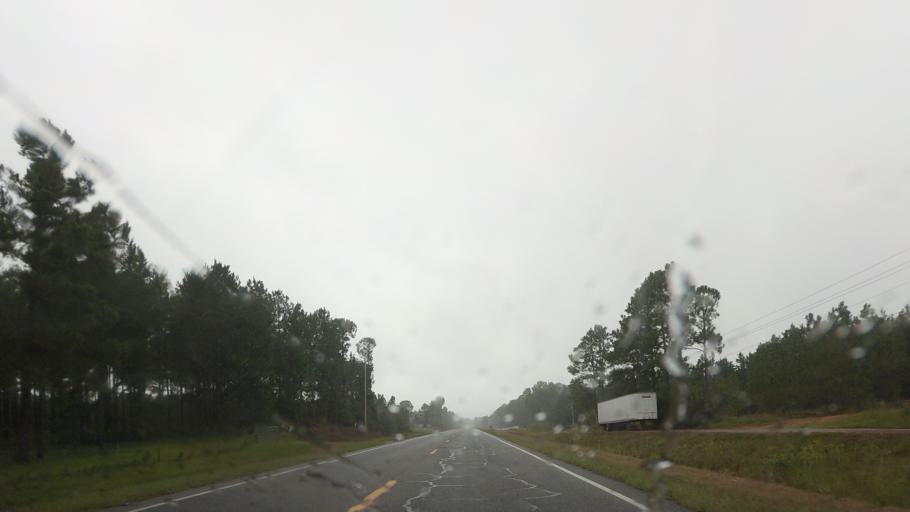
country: US
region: Georgia
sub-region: Ben Hill County
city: Fitzgerald
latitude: 31.7535
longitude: -83.2459
